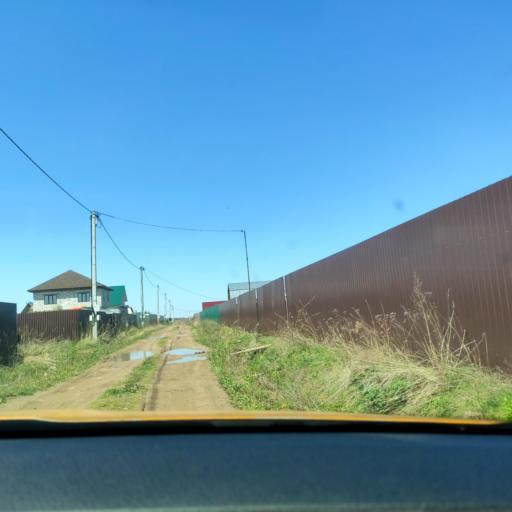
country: RU
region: Moskovskaya
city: Beloozerskiy
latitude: 55.3722
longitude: 38.4021
